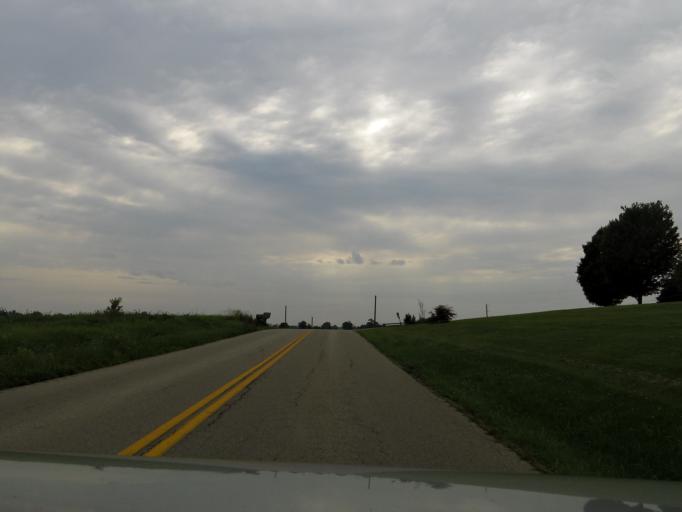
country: US
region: Kentucky
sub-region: Robertson County
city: Mount Olivet
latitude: 38.5098
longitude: -83.8866
